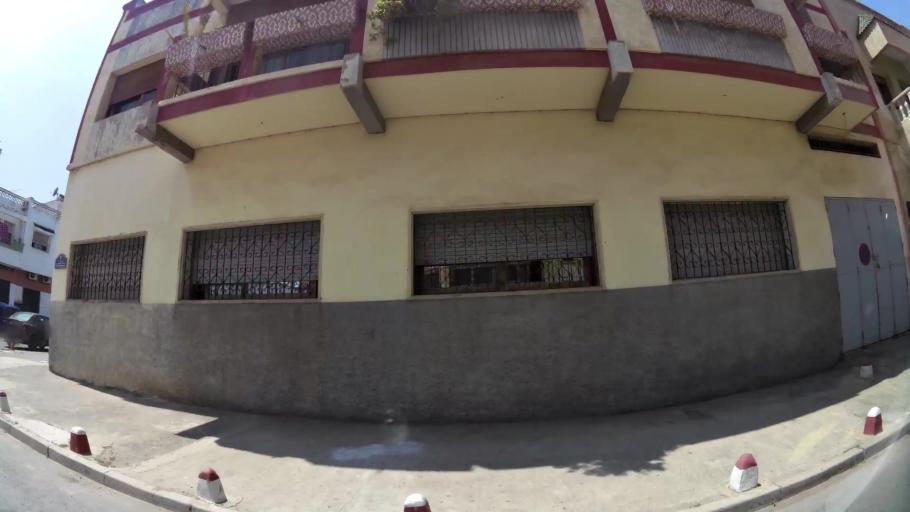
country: MA
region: Rabat-Sale-Zemmour-Zaer
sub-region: Skhirate-Temara
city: Temara
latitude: 33.9745
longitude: -6.8926
